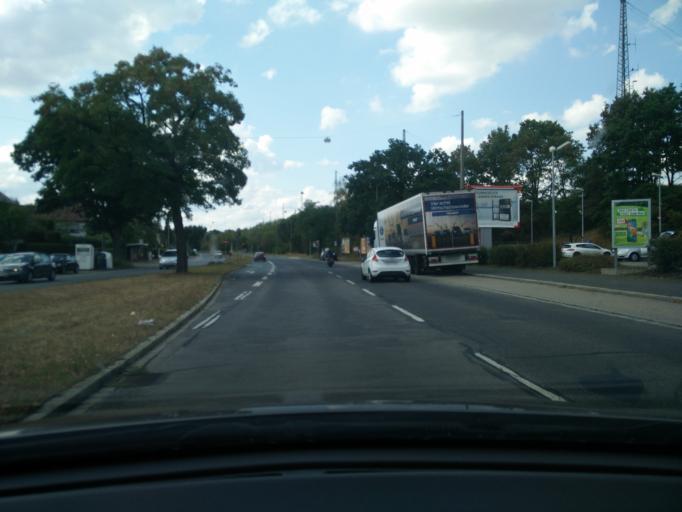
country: DE
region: Bavaria
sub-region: Regierungsbezirk Mittelfranken
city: Nuernberg
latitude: 49.4063
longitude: 11.1104
